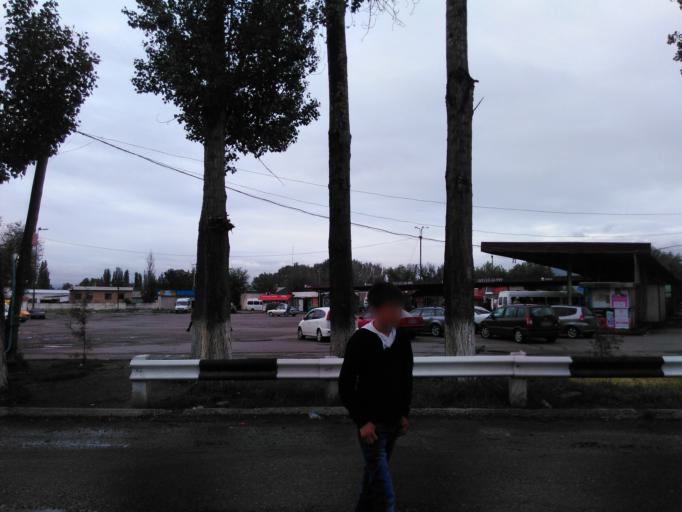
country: KG
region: Chuy
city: Chuy
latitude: 42.8299
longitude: 75.2891
